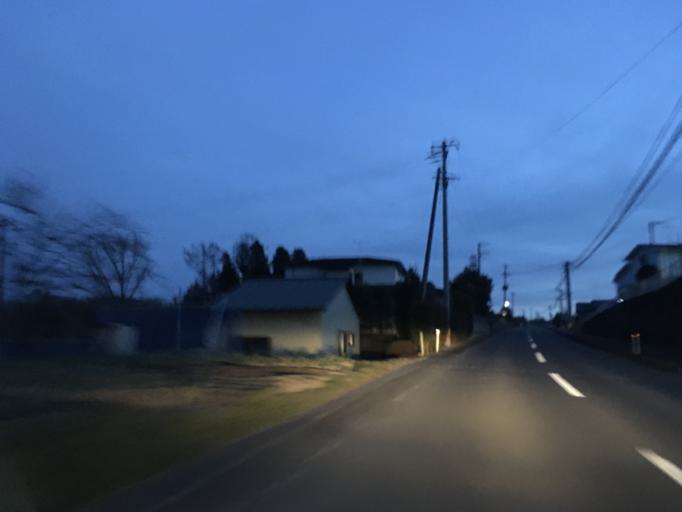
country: JP
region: Miyagi
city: Wakuya
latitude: 38.6965
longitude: 141.1631
